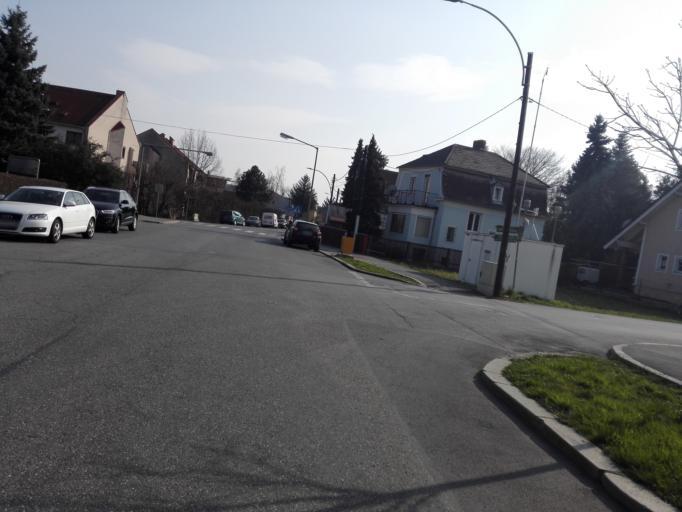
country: AT
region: Styria
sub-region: Graz Stadt
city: Graz
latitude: 47.0419
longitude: 15.4332
